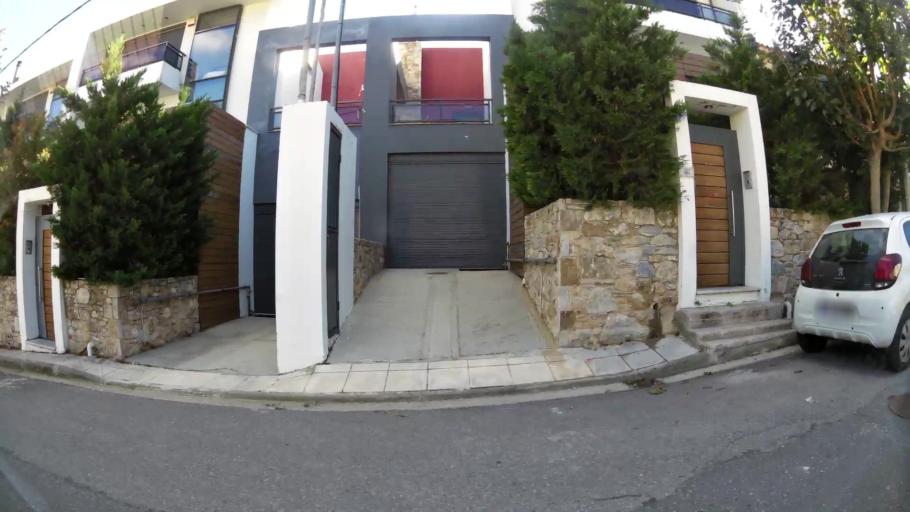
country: GR
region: Attica
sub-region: Nomarchia Anatolikis Attikis
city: Anthousa
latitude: 38.0275
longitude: 23.8776
